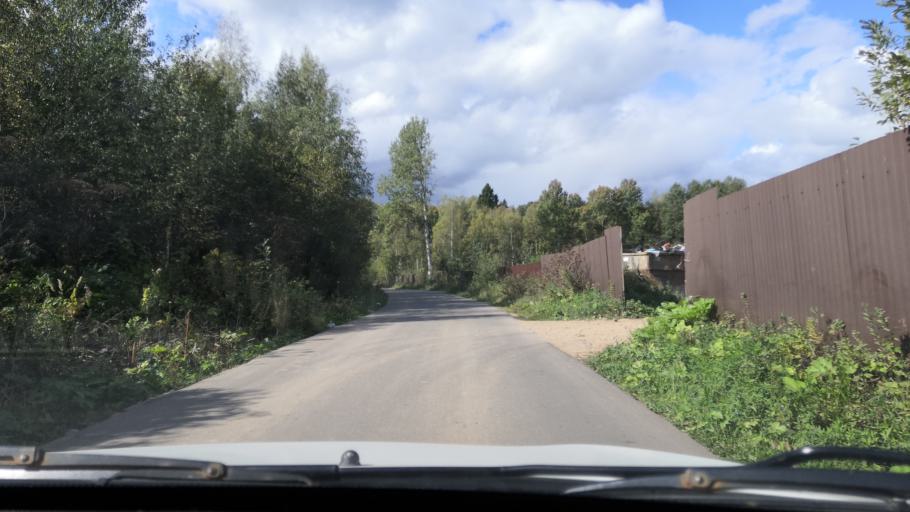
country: RU
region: Moskovskaya
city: Povarovo
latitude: 56.0647
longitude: 37.0382
